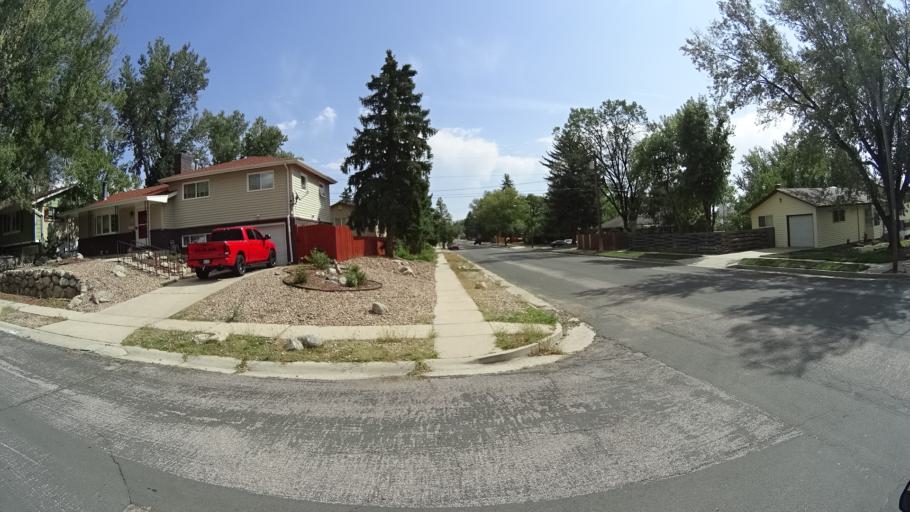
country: US
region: Colorado
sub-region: El Paso County
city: Colorado Springs
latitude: 38.8617
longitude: -104.7680
